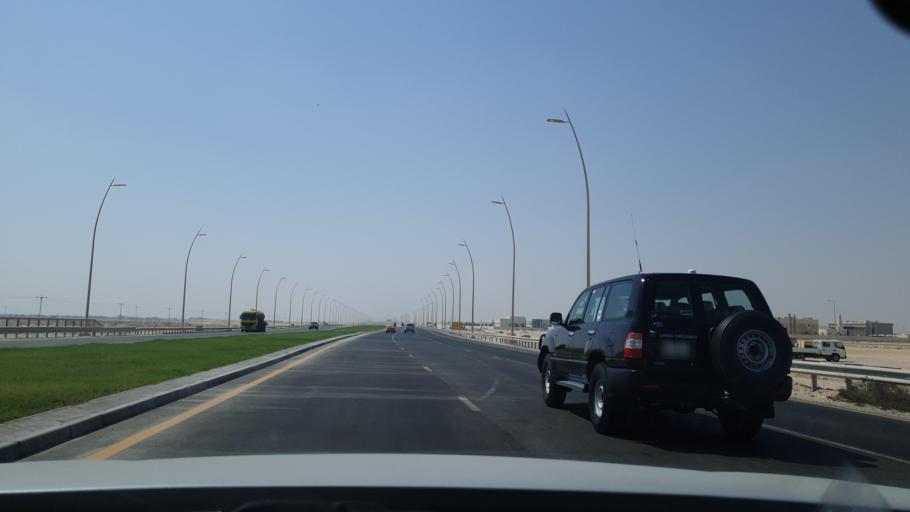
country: QA
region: Al Khawr
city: Al Khawr
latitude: 25.6642
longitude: 51.4732
